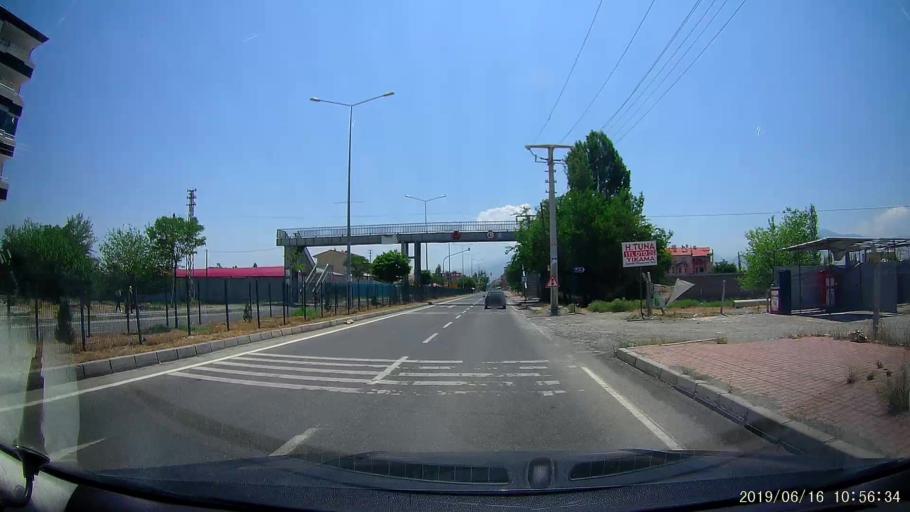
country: TR
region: Igdir
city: Igdir
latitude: 39.9286
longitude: 44.0244
